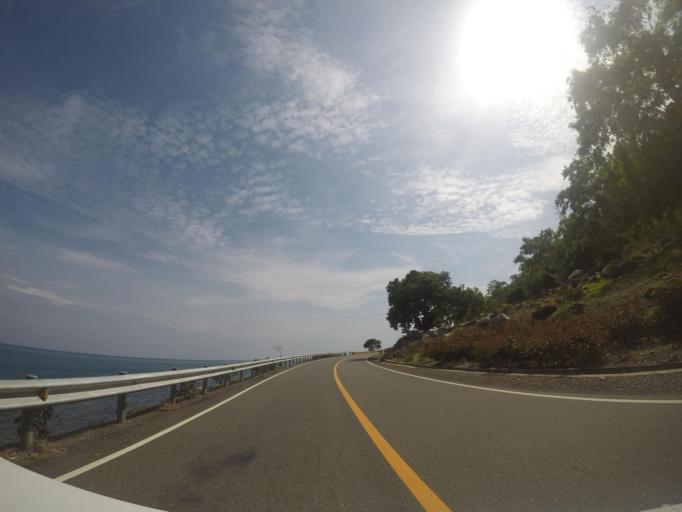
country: TL
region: Manatuto
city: Manatuto
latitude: -8.4798
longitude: 125.9268
